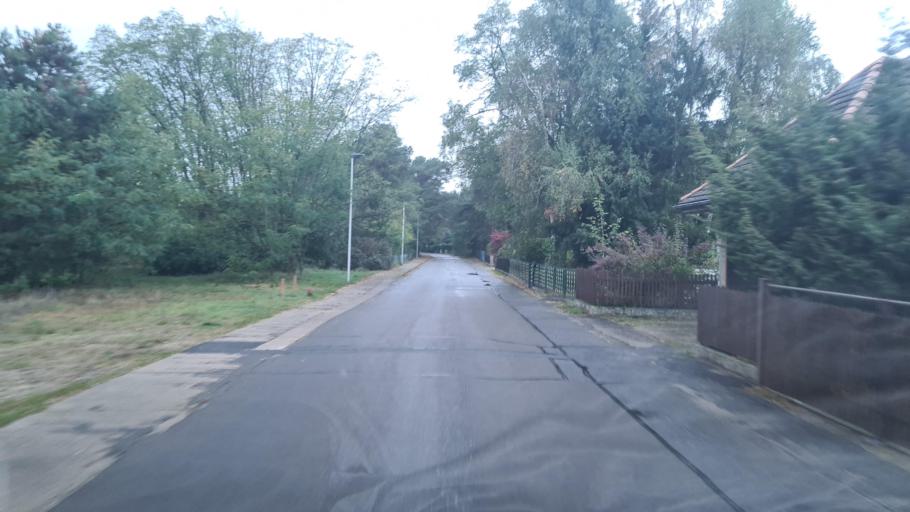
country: DE
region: Brandenburg
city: Munchehofe
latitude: 52.1246
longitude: 13.9474
